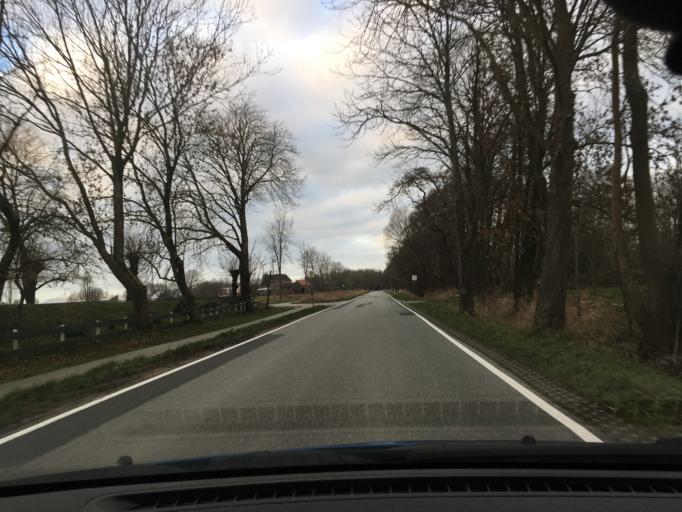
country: DE
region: Schleswig-Holstein
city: Norderwohrden
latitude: 54.1945
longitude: 9.0350
